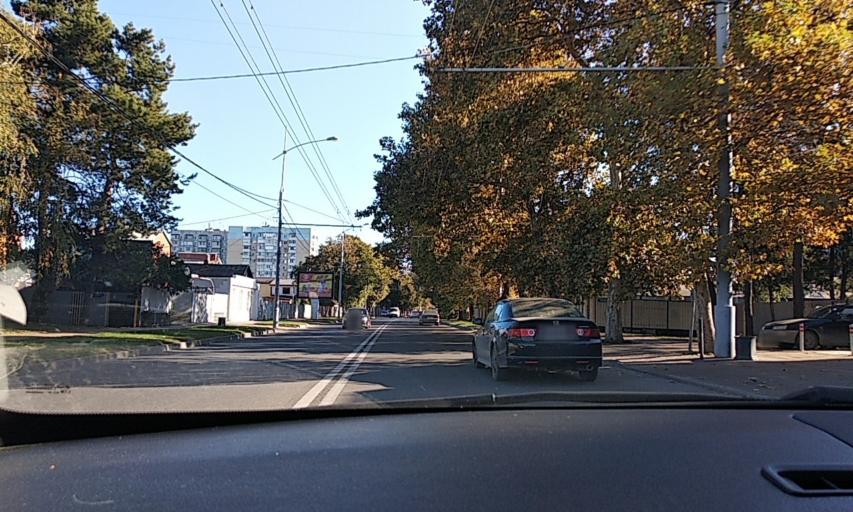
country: RU
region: Krasnodarskiy
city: Pashkovskiy
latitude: 45.0280
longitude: 39.1202
